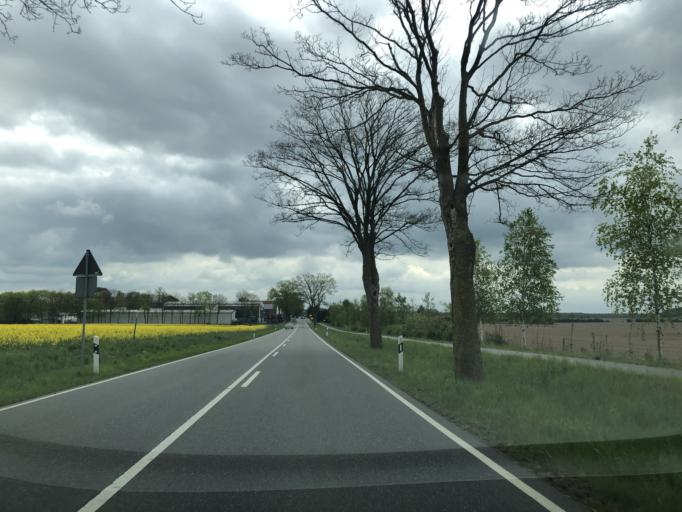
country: DE
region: Mecklenburg-Vorpommern
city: Plau am See
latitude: 53.4614
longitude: 12.2184
